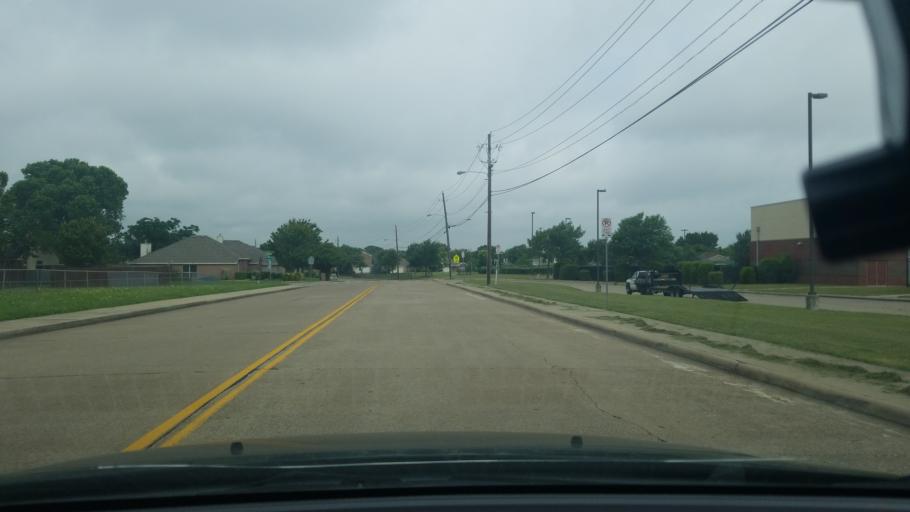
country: US
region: Texas
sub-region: Dallas County
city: Balch Springs
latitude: 32.7838
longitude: -96.6916
